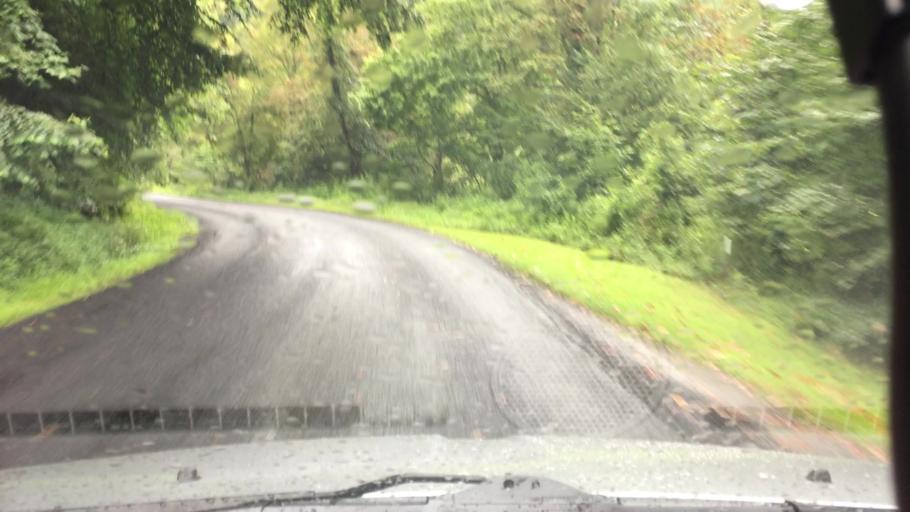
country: US
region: North Carolina
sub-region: Madison County
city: Mars Hill
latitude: 35.9109
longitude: -82.5304
